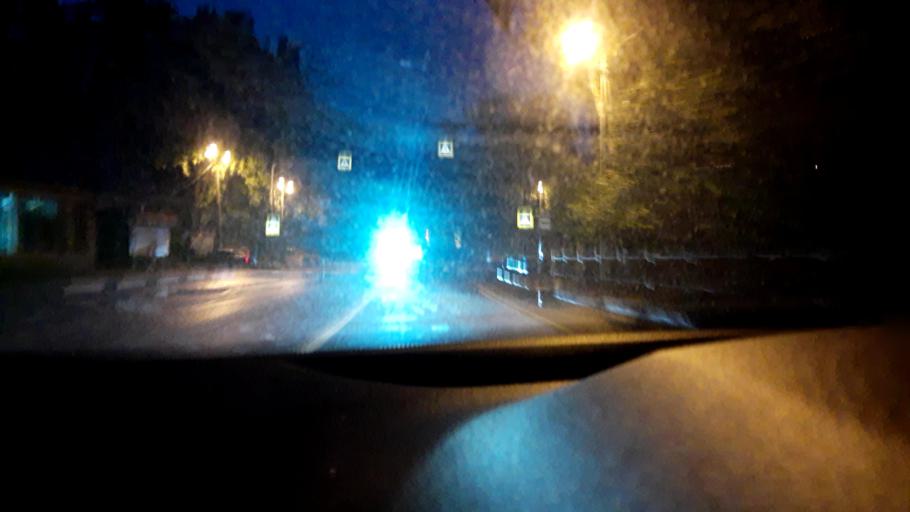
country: RU
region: Moskovskaya
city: Petrovo-Dal'neye
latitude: 55.7905
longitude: 37.2062
